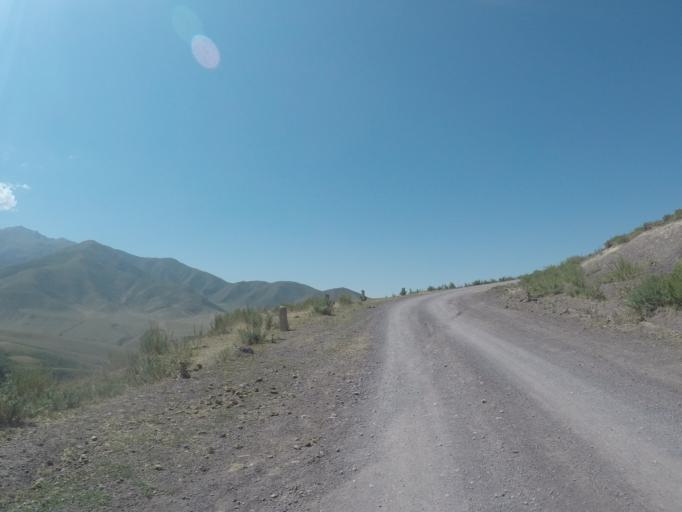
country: KG
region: Chuy
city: Bishkek
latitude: 42.6509
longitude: 74.5160
